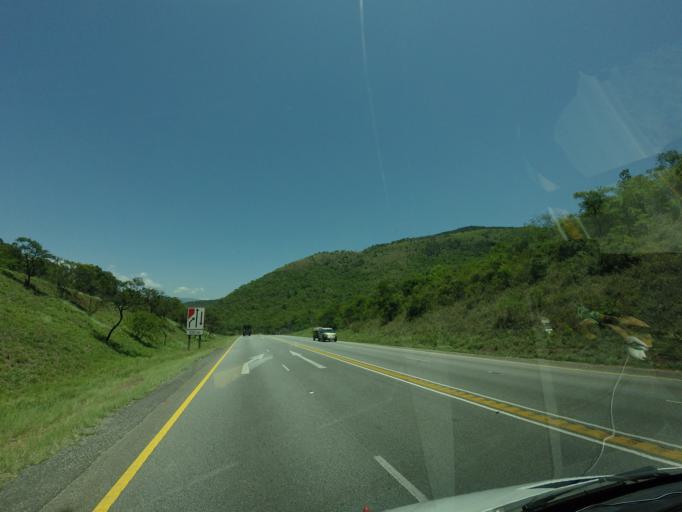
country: ZA
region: Mpumalanga
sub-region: Ehlanzeni District
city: Nelspruit
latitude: -25.4450
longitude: 30.7187
